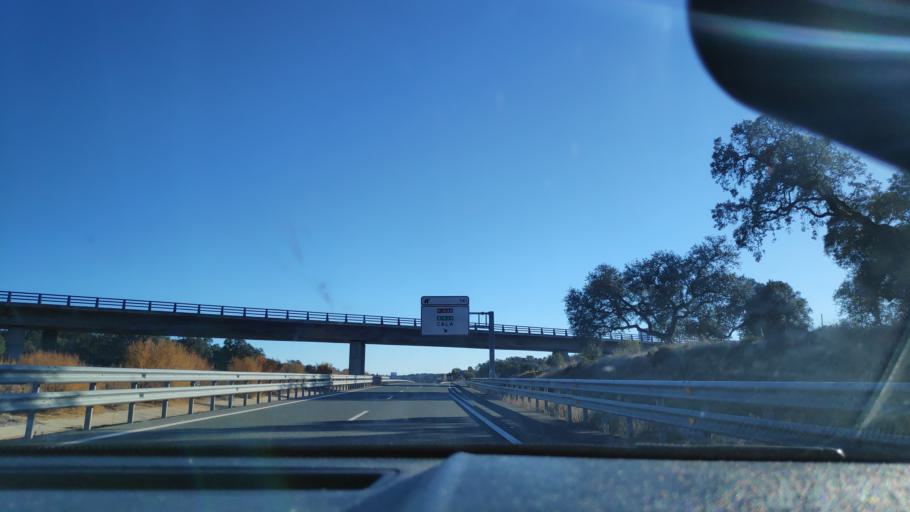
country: ES
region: Andalusia
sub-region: Provincia de Huelva
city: Santa Olalla del Cala
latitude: 37.9514
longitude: -6.2307
